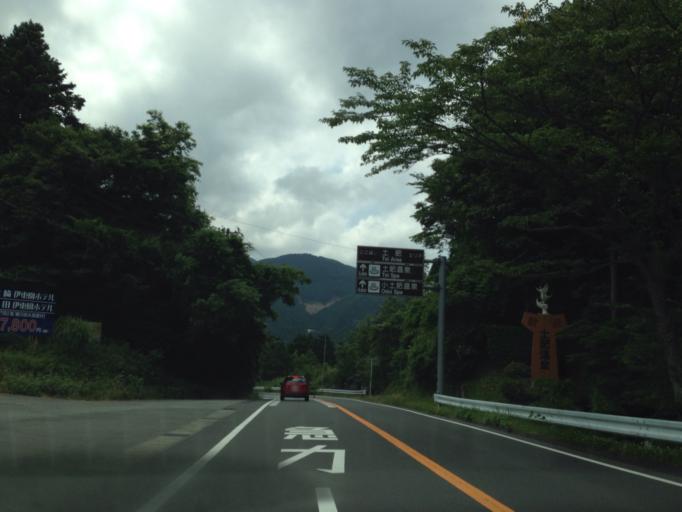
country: JP
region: Shizuoka
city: Heda
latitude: 34.9120
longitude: 138.8121
